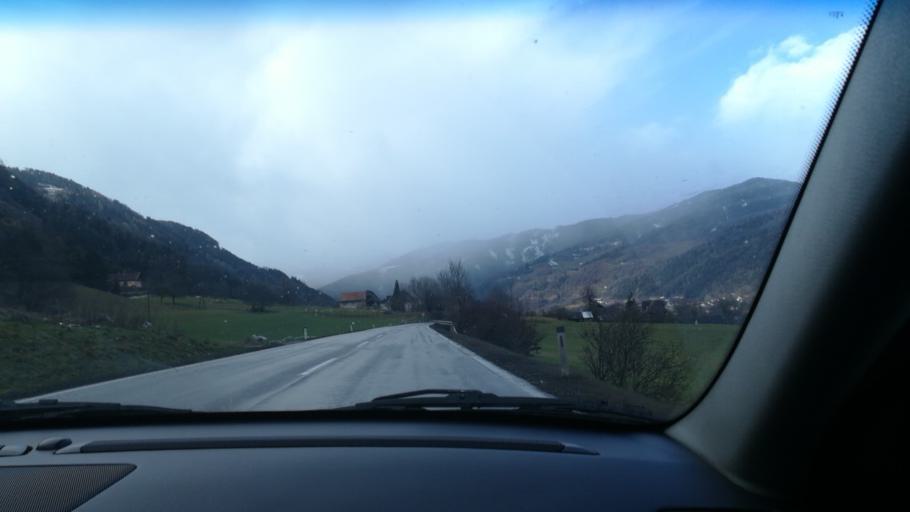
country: AT
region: Styria
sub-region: Politischer Bezirk Murtal
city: Sankt Georgen ob Judenburg
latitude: 47.2015
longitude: 14.5157
